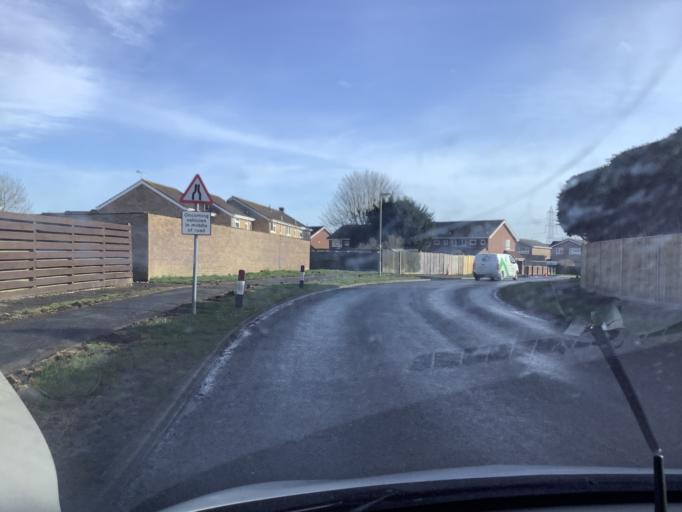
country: GB
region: England
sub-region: Hampshire
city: Hythe
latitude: 50.8282
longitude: -1.3920
